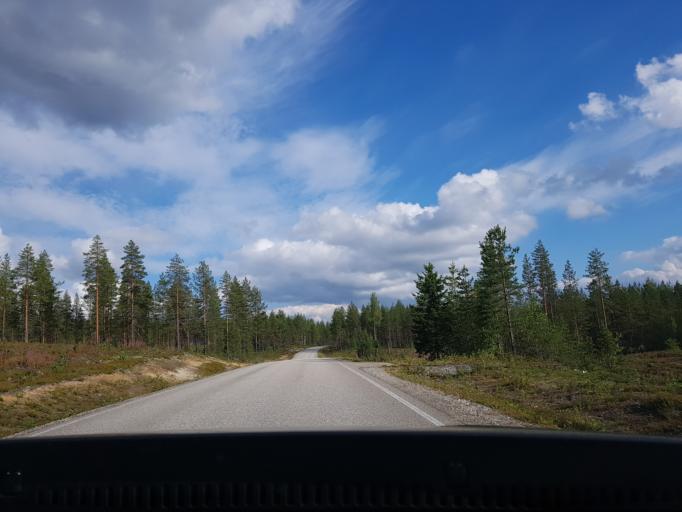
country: FI
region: Kainuu
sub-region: Kehys-Kainuu
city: Kuhmo
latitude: 64.6201
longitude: 29.7039
